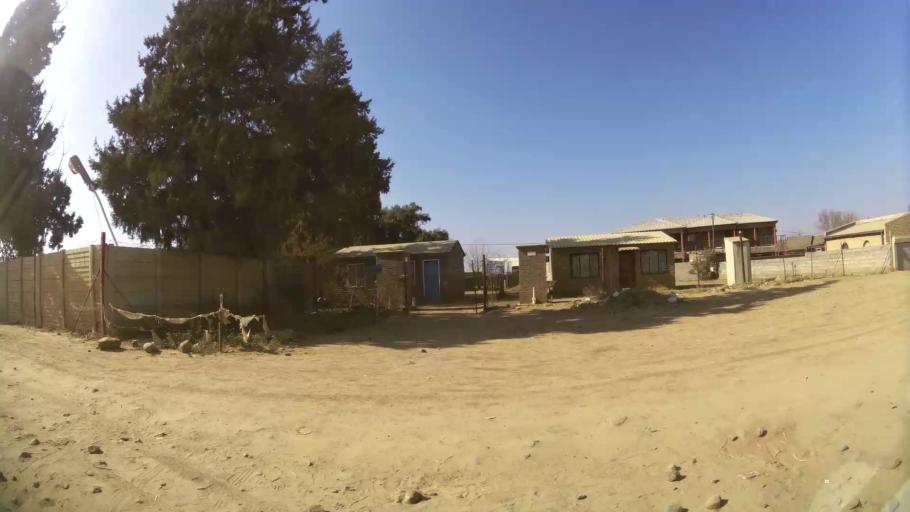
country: ZA
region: Orange Free State
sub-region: Mangaung Metropolitan Municipality
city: Bloemfontein
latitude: -29.1920
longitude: 26.2827
